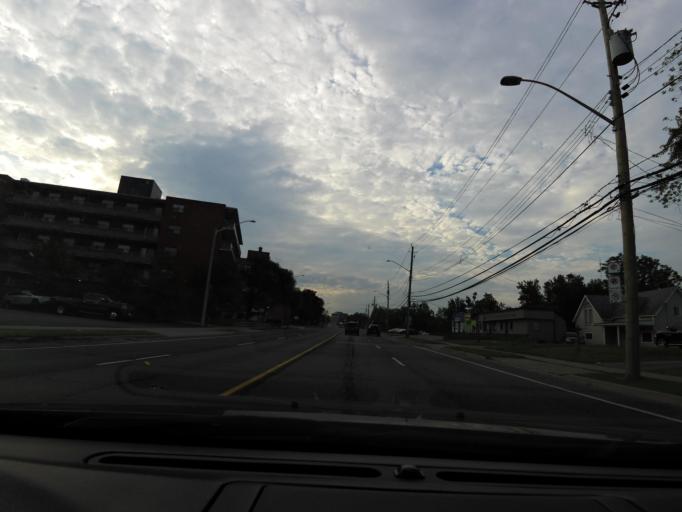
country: CA
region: Ontario
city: Hamilton
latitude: 43.2236
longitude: -79.7838
